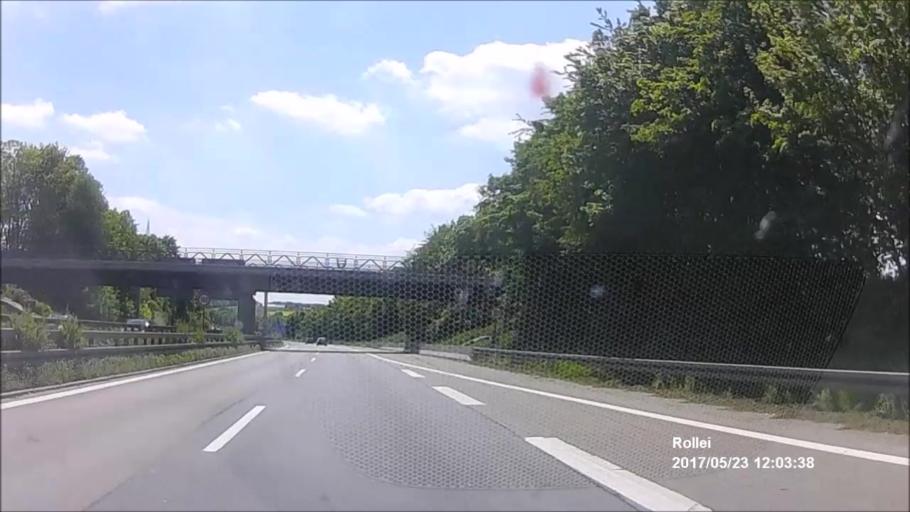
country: DE
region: Bavaria
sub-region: Upper Palatinate
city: Pentling
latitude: 48.9886
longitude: 12.0605
